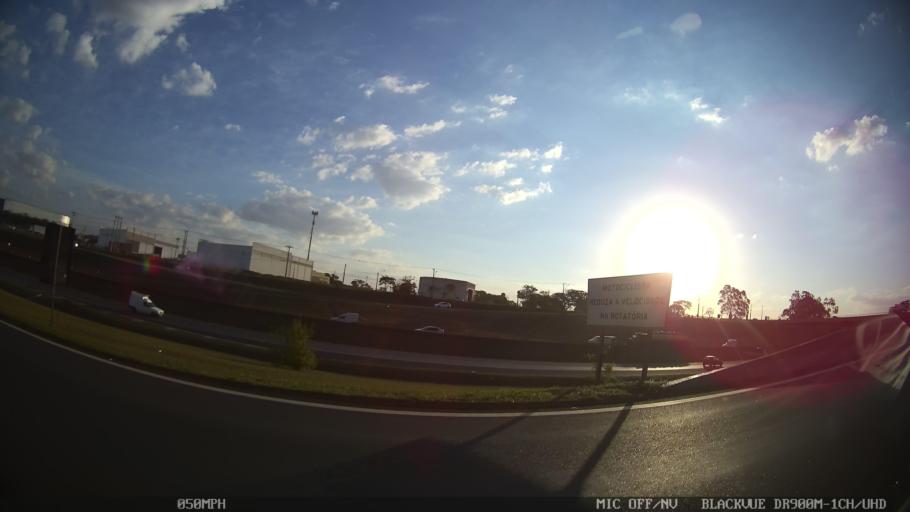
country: BR
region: Sao Paulo
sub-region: Ribeirao Preto
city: Ribeirao Preto
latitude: -21.1503
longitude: -47.7574
